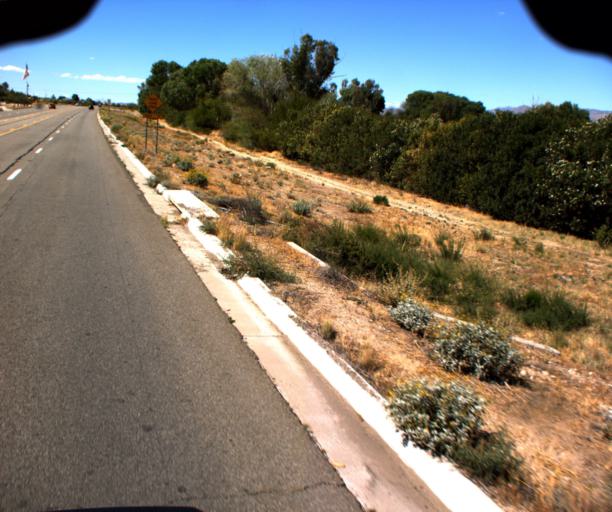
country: US
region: Arizona
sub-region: Yavapai County
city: Bagdad
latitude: 34.7095
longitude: -113.6131
